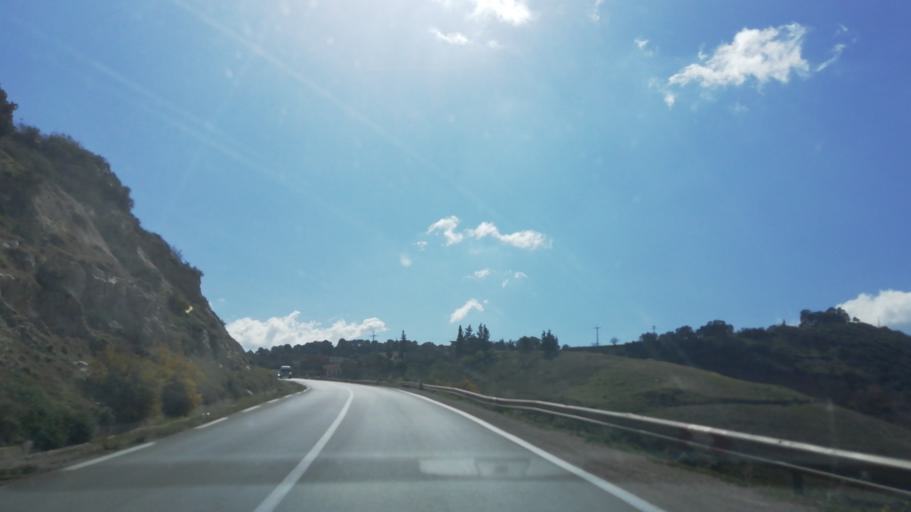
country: DZ
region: Mascara
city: Mascara
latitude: 35.4615
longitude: 0.1485
